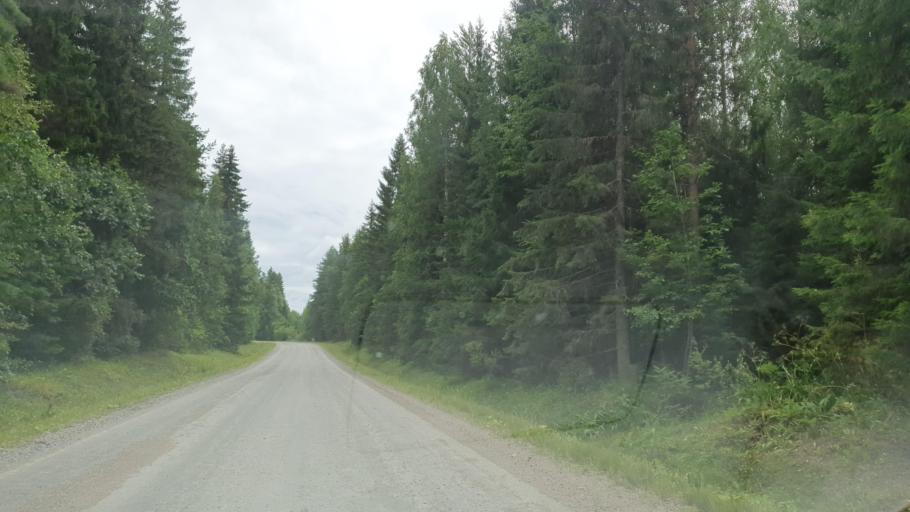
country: FI
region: Northern Savo
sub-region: Ylae-Savo
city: Iisalmi
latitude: 63.5397
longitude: 27.0730
